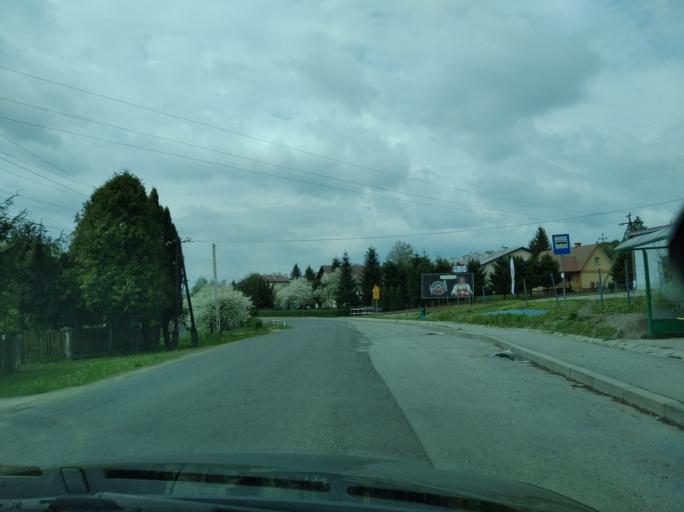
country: PL
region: Subcarpathian Voivodeship
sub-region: Powiat brzozowski
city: Jasionow
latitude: 49.6446
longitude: 21.9463
